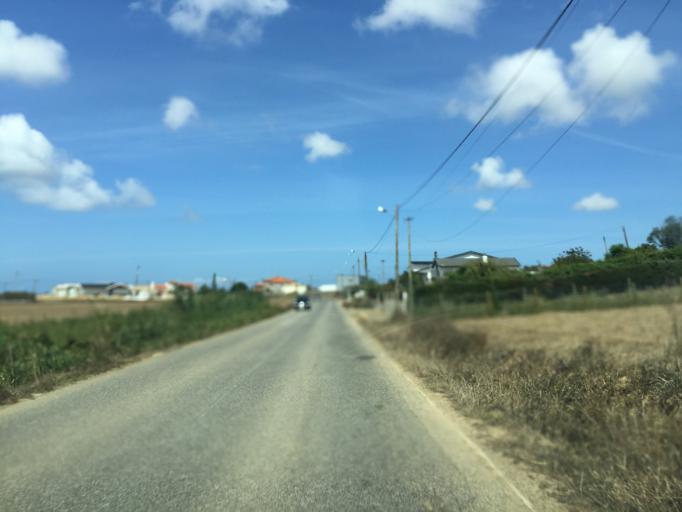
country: PT
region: Leiria
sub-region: Peniche
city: Atouguia da Baleia
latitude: 39.2908
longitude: -9.3079
